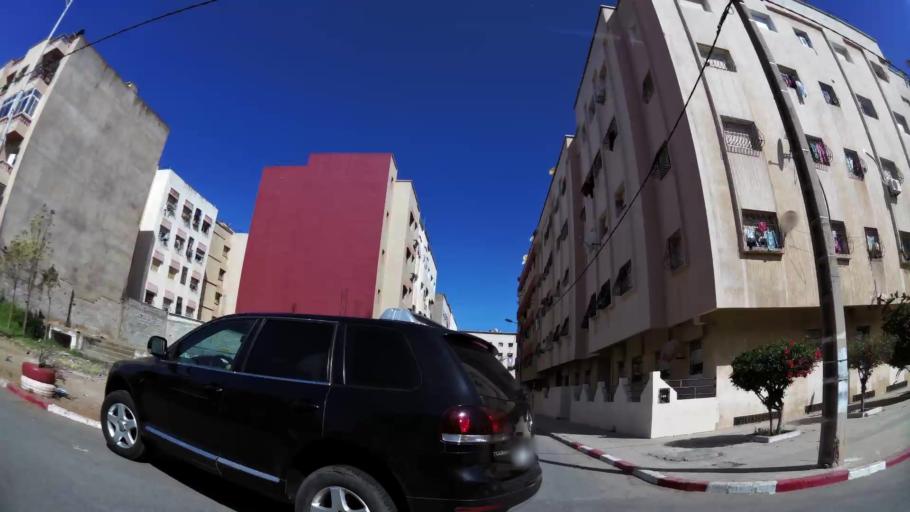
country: MA
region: Rabat-Sale-Zemmour-Zaer
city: Sale
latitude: 34.0671
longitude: -6.8006
